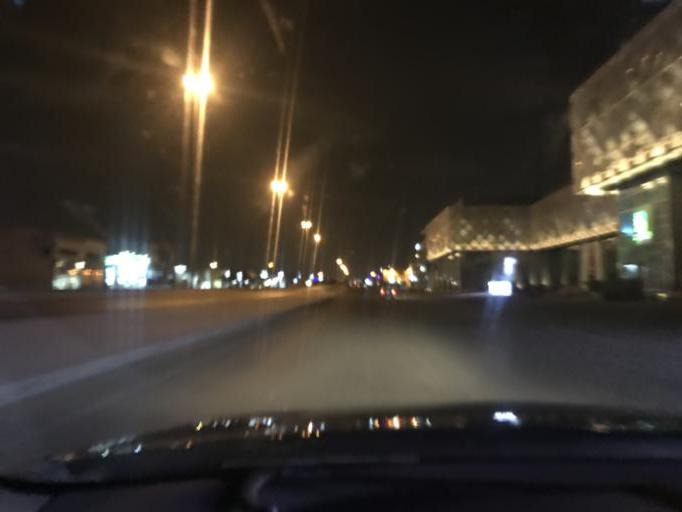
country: SA
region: Ar Riyad
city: Riyadh
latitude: 24.7964
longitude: 46.6984
